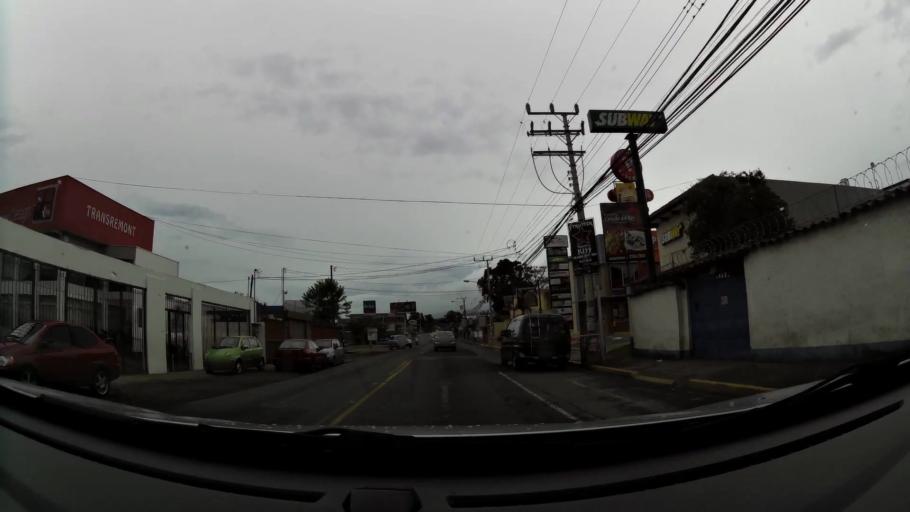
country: CR
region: San Jose
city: San Juan
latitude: 9.9712
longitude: -84.0887
